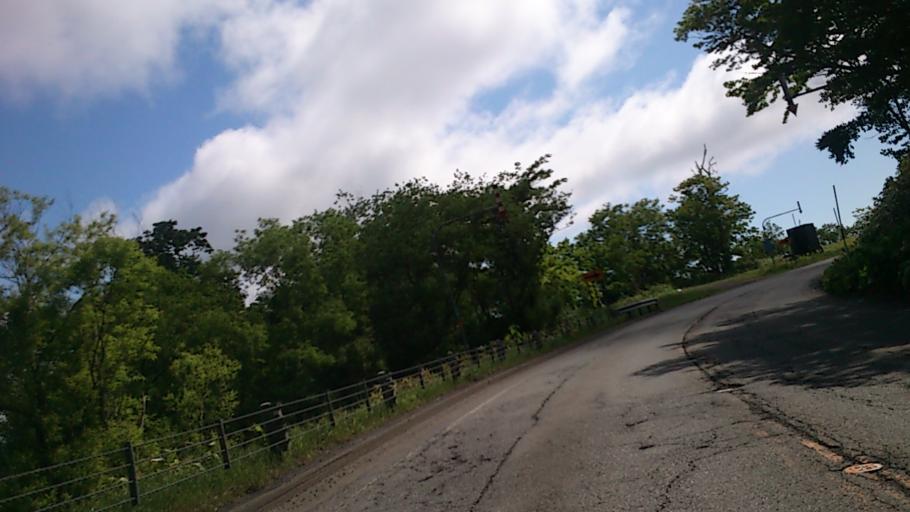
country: JP
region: Hokkaido
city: Shiraoi
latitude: 42.7172
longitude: 141.2044
